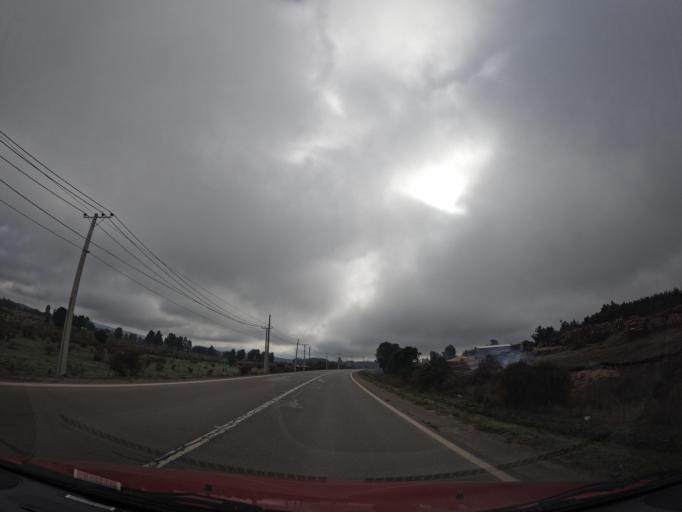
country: CL
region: Maule
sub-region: Provincia de Cauquenes
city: Cauquenes
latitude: -36.2681
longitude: -72.5473
